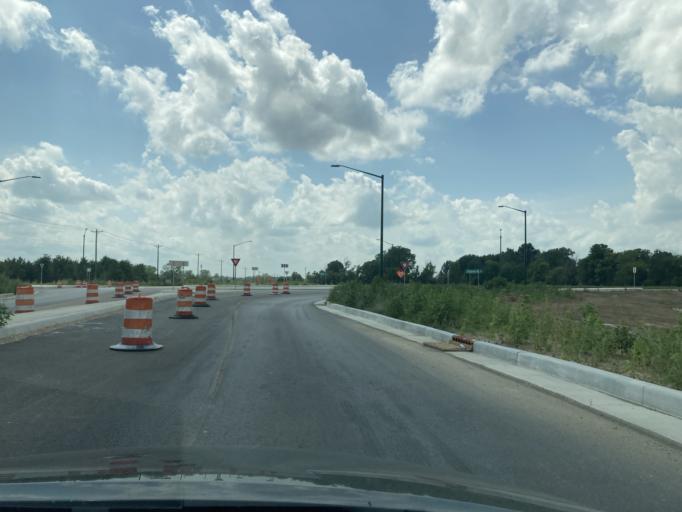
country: US
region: Indiana
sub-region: Boone County
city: Zionsville
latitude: 39.9993
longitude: -86.2208
